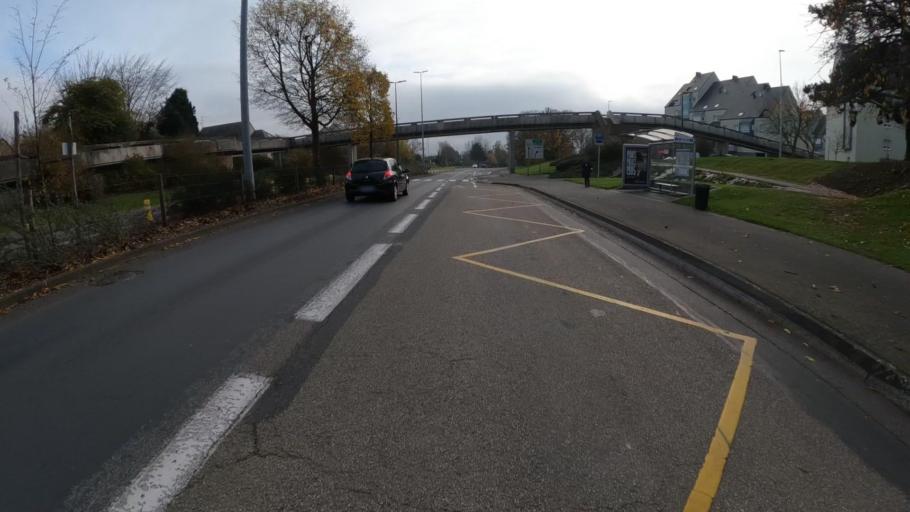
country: FR
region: Lower Normandy
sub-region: Departement du Calvados
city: Epron
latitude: 49.2052
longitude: -0.3759
